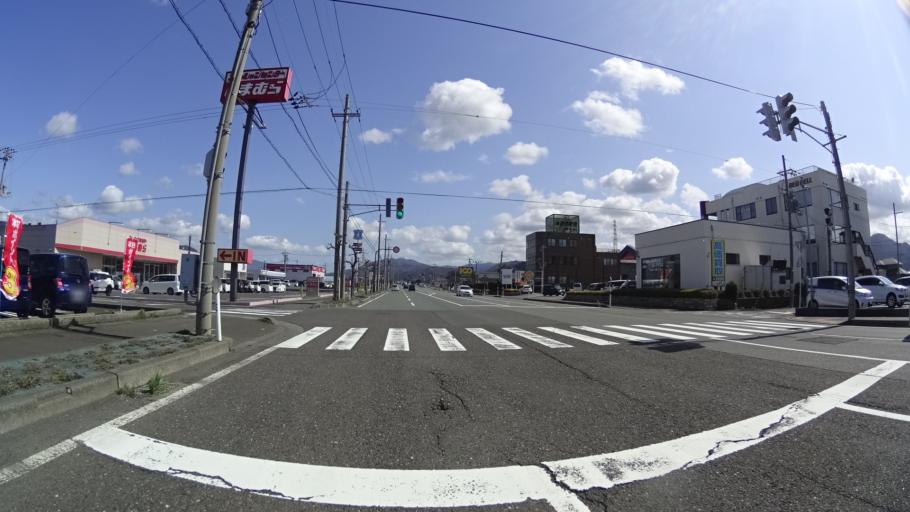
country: JP
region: Fukui
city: Obama
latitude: 35.4946
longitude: 135.7582
